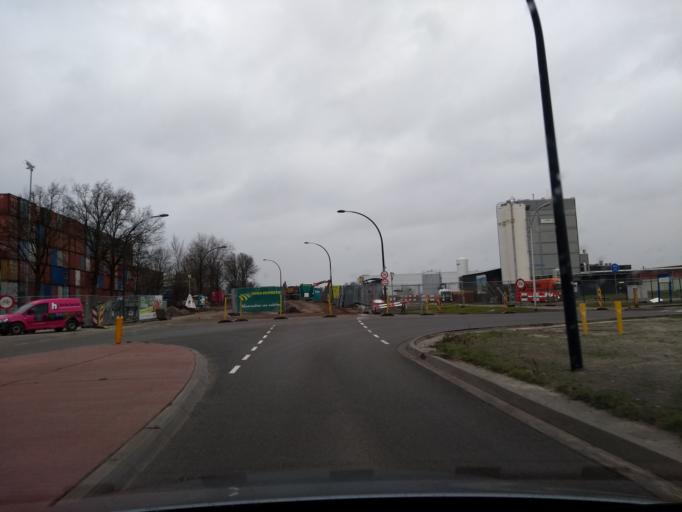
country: NL
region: Overijssel
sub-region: Gemeente Hengelo
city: Hengelo
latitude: 52.2454
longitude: 6.7887
